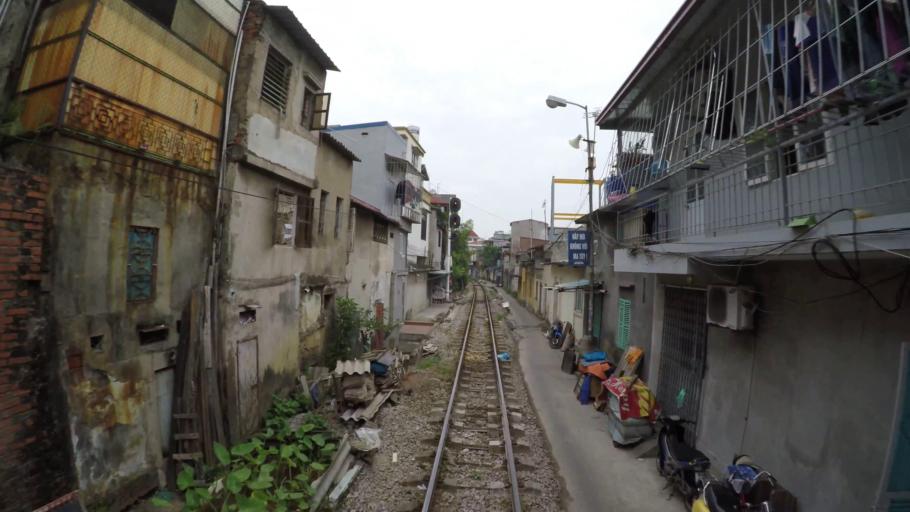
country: VN
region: Hai Phong
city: Haiphong
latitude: 20.8531
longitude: 106.6670
